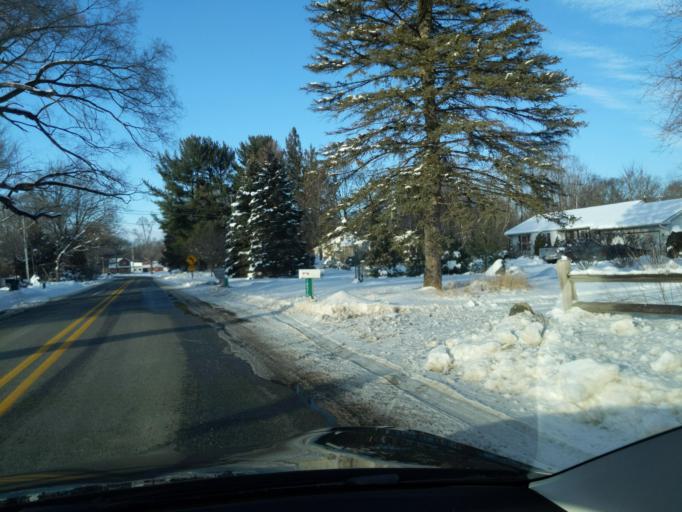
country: US
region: Michigan
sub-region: Ingham County
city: Stockbridge
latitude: 42.4397
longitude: -84.0967
